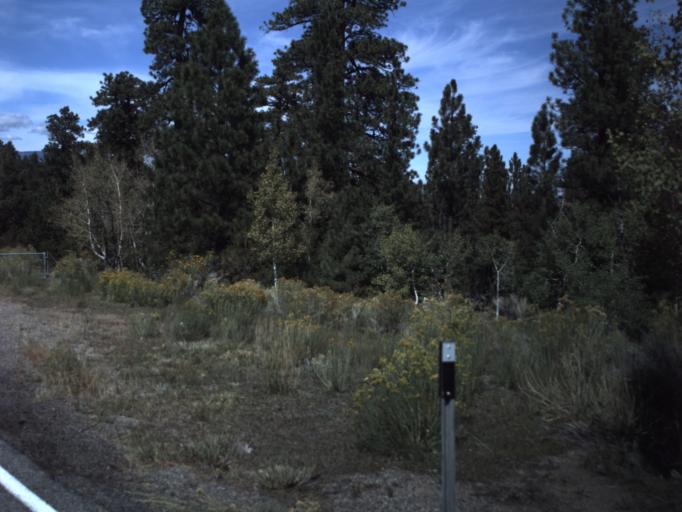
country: US
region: Utah
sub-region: Wayne County
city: Loa
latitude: 38.1861
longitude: -111.3520
